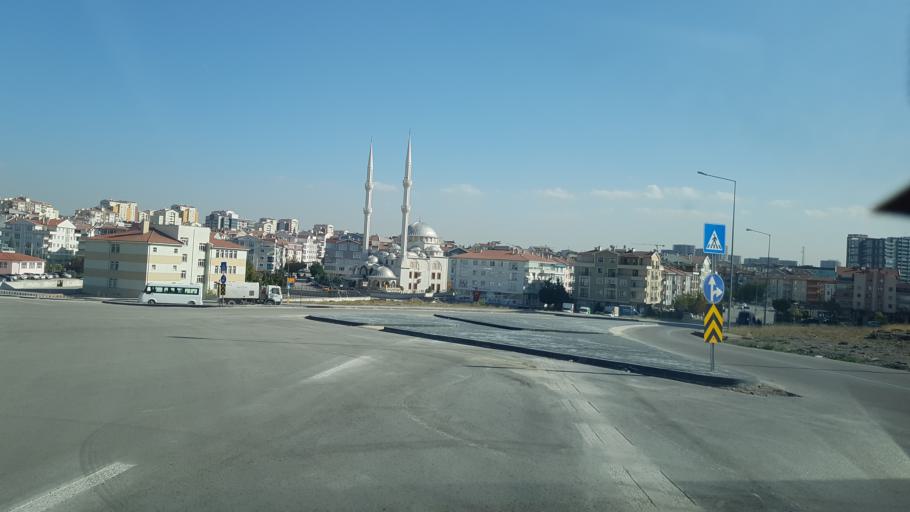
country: TR
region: Ankara
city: Etimesgut
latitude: 39.9730
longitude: 32.6111
